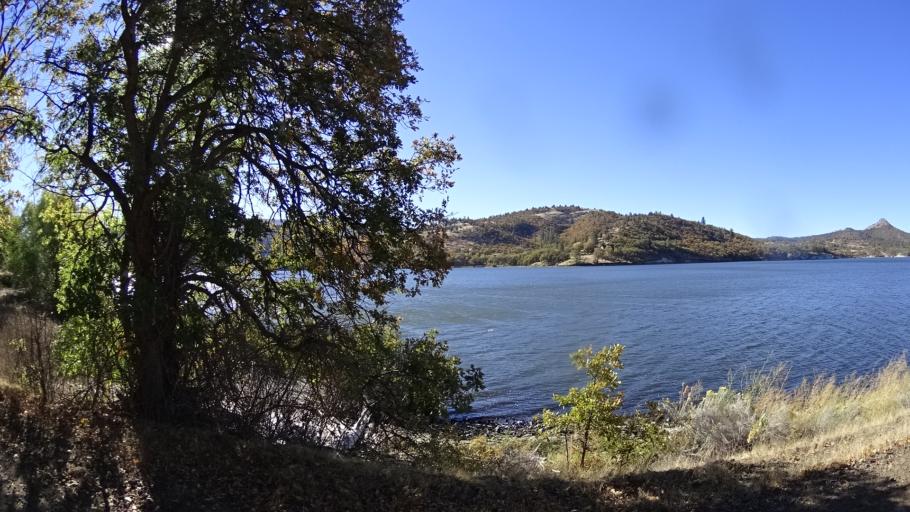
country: US
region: California
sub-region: Siskiyou County
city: Montague
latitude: 41.9867
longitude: -122.3069
